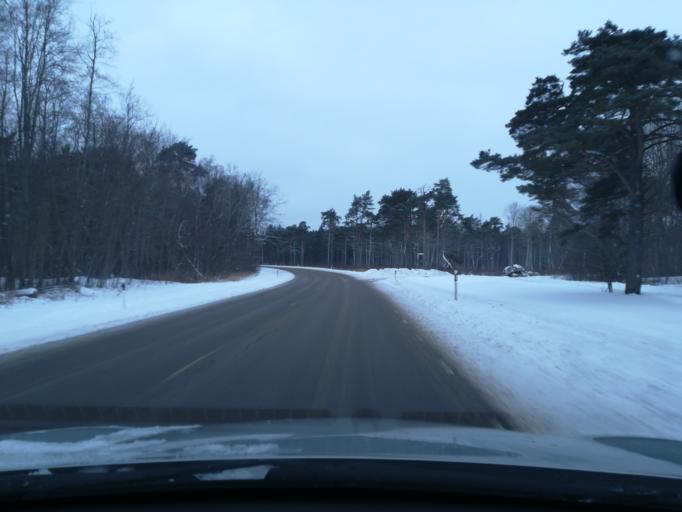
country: EE
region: Harju
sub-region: Keila linn
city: Keila
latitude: 59.4013
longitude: 24.3018
